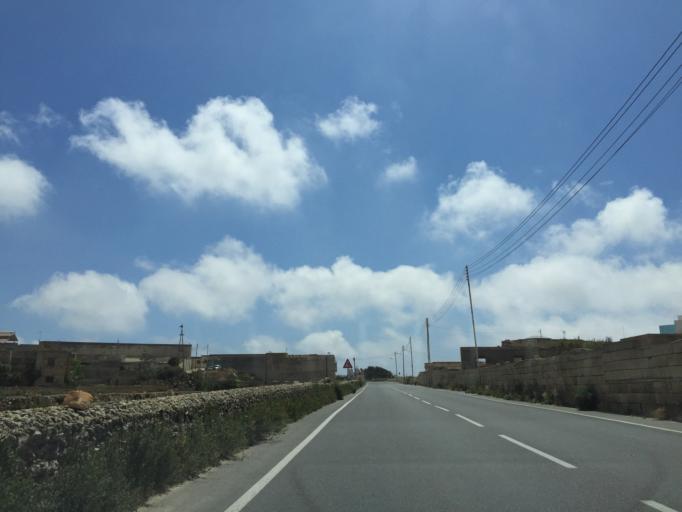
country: MT
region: Ir-Rabat
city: Rabat
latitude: 35.8717
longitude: 14.3926
